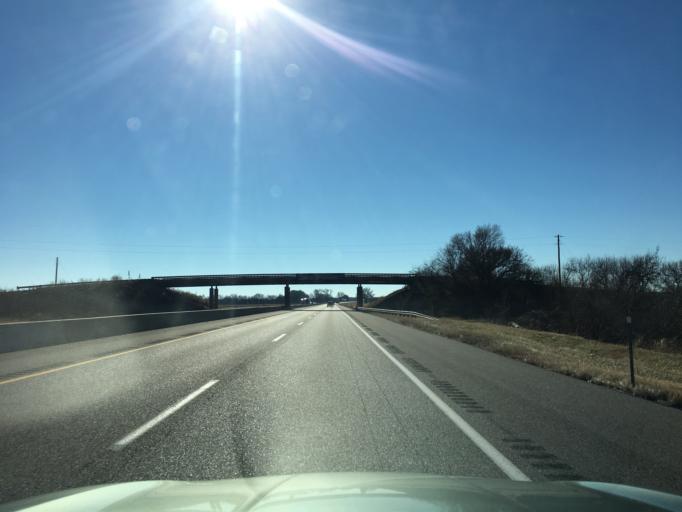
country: US
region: Kansas
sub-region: Sumner County
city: Belle Plaine
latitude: 37.4224
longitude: -97.3213
